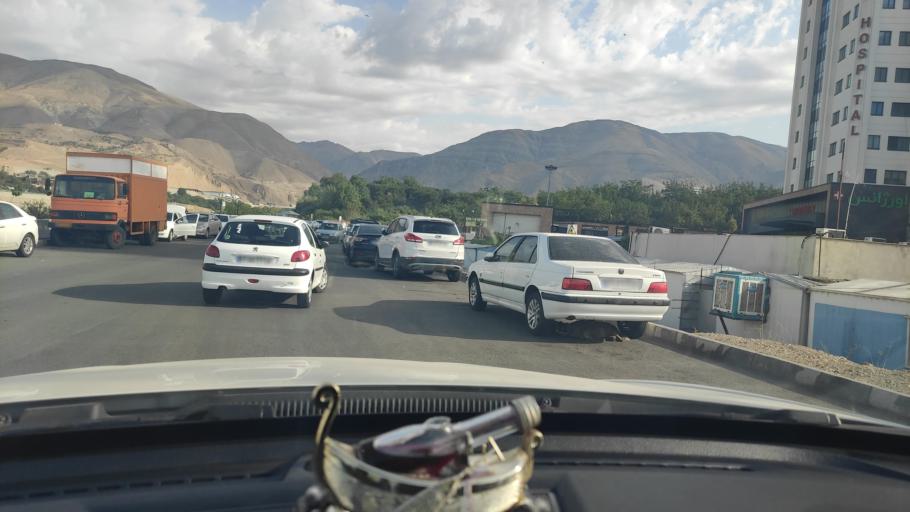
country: IR
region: Tehran
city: Tajrish
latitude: 35.7561
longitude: 51.2696
